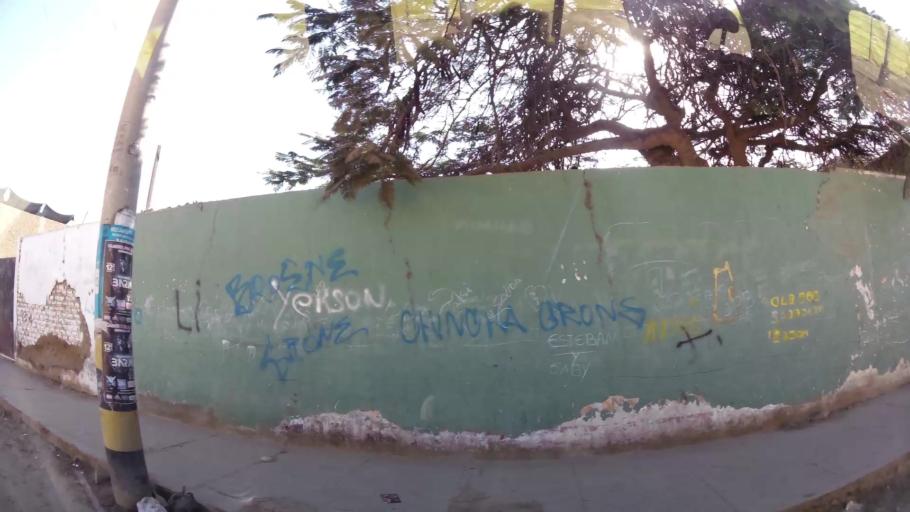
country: PE
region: Ica
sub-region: Provincia de Chincha
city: Chincha Alta
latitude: -13.4203
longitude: -76.1366
